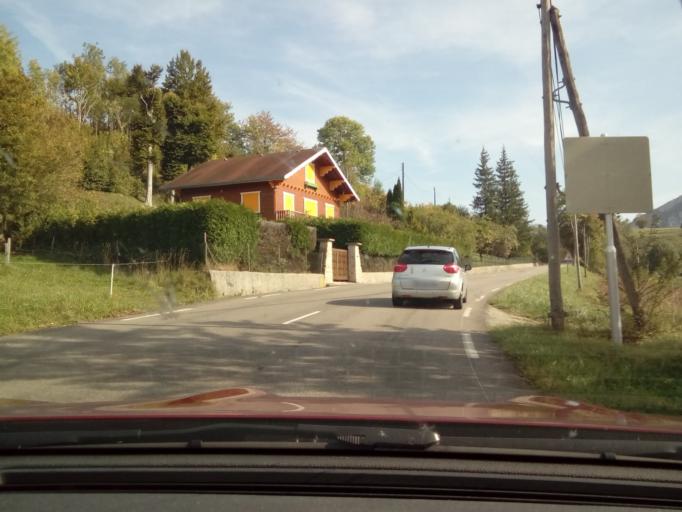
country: FR
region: Rhone-Alpes
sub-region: Departement de la Drome
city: Saint-Laurent-en-Royans
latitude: 44.9714
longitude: 5.4065
